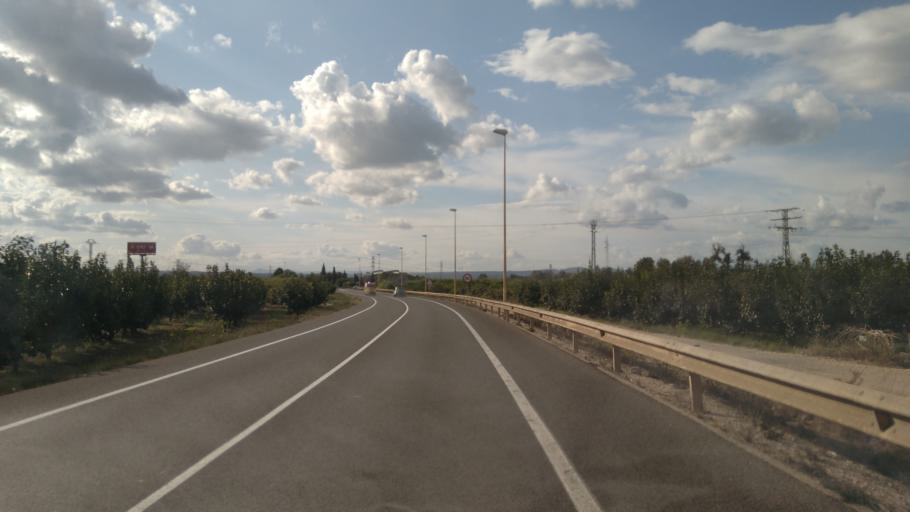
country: ES
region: Valencia
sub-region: Provincia de Valencia
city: Alzira
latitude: 39.1638
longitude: -0.4417
